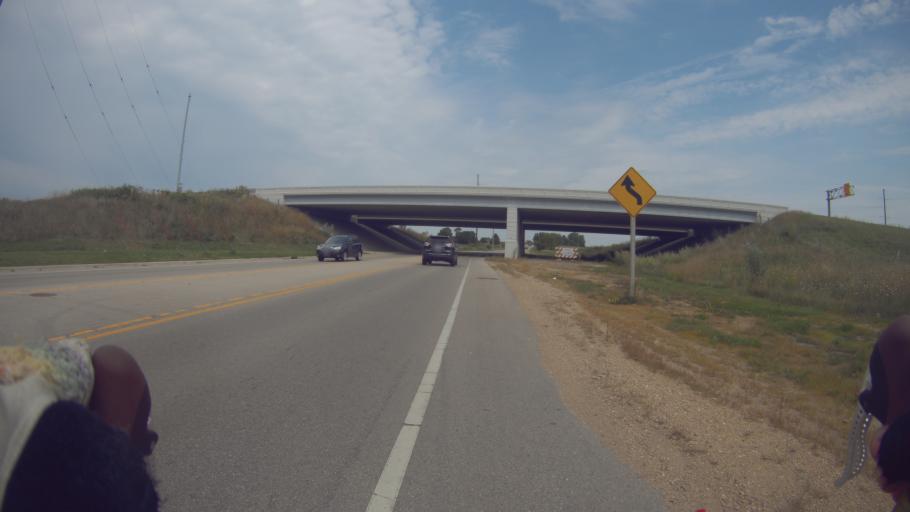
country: US
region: Wisconsin
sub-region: Dane County
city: Cottage Grove
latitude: 43.1029
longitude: -89.2667
